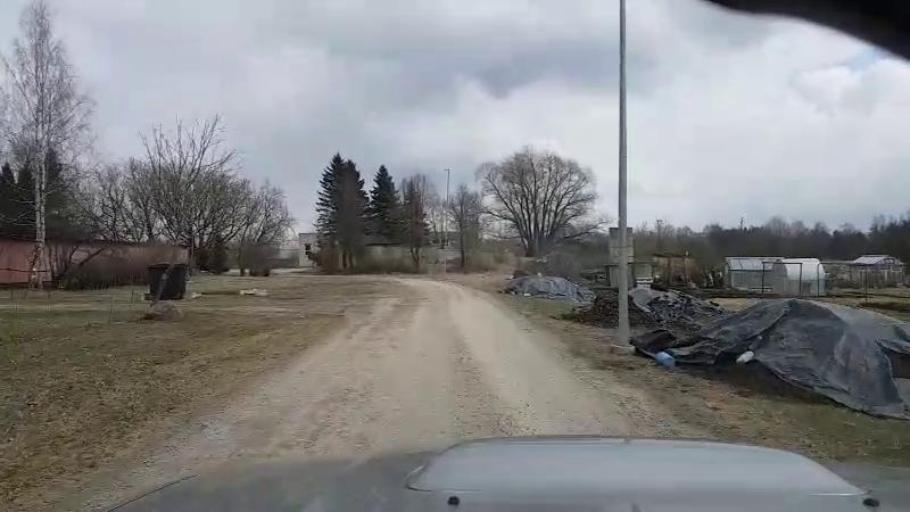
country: EE
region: Jaervamaa
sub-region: Paide linn
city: Paide
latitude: 58.8802
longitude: 25.5713
